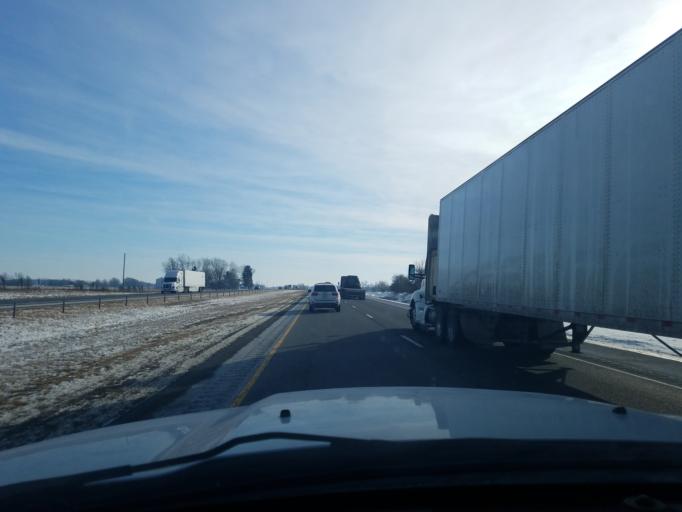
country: US
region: Indiana
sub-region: Grant County
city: Fairmount
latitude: 40.3257
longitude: -85.5590
